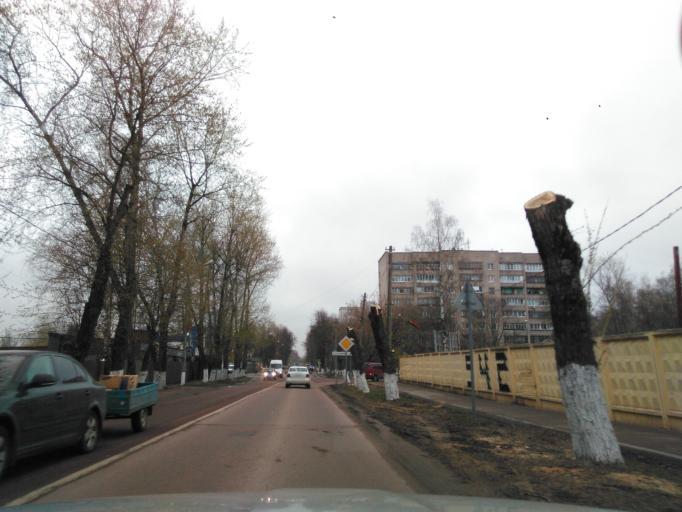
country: RU
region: Moskovskaya
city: Nakhabino
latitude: 55.8405
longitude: 37.1693
